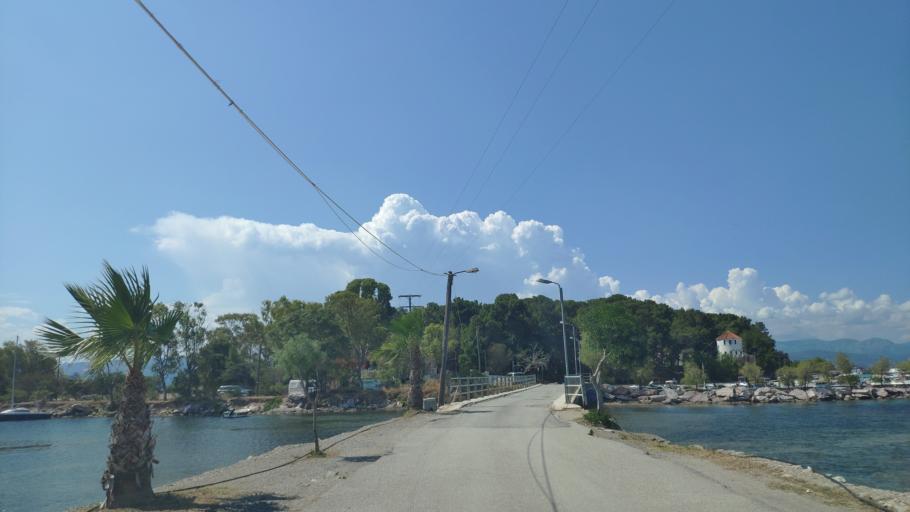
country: GR
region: Central Greece
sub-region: Nomos Evvoias
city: Eretria
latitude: 38.3869
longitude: 23.8009
